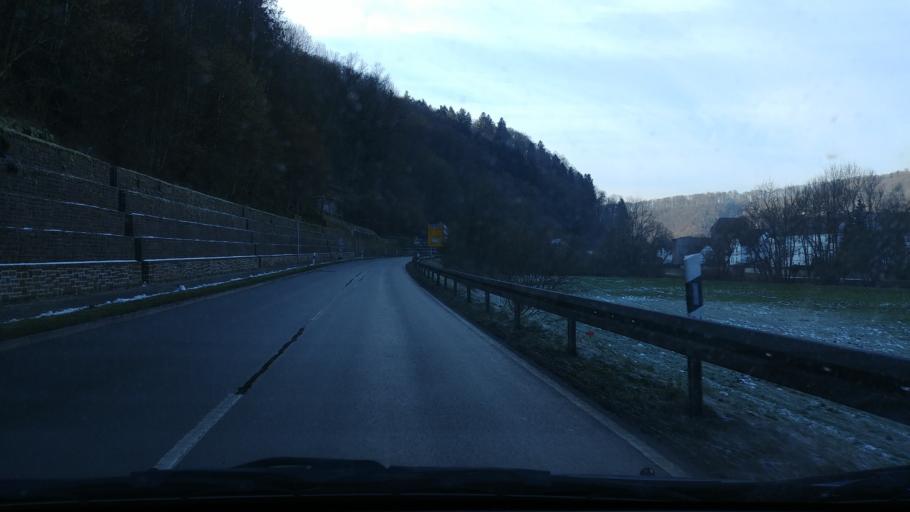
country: DE
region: Lower Saxony
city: Bad Karlshafen
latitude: 51.6382
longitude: 9.4536
